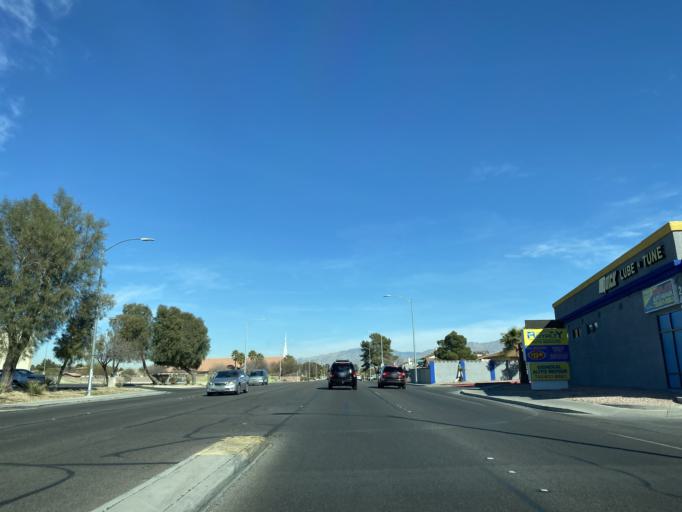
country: US
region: Nevada
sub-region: Clark County
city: Las Vegas
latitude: 36.2037
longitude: -115.2238
